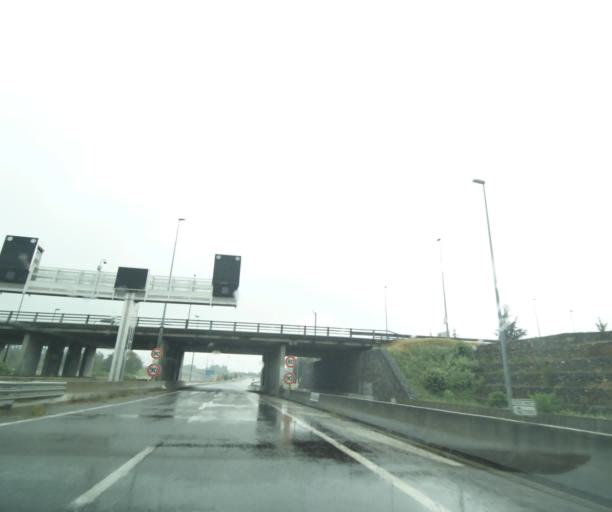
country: FR
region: Midi-Pyrenees
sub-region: Departement de la Haute-Garonne
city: Ramonville-Saint-Agne
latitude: 43.5581
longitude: 1.4901
